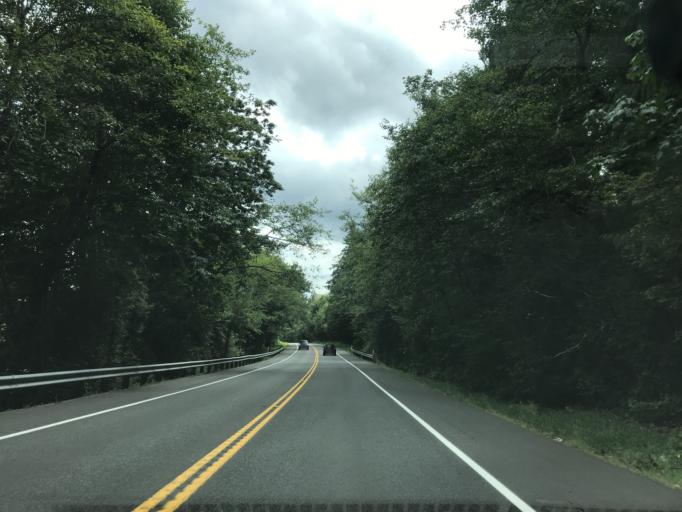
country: US
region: Washington
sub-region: King County
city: Maple Valley
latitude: 47.4161
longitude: -122.0655
